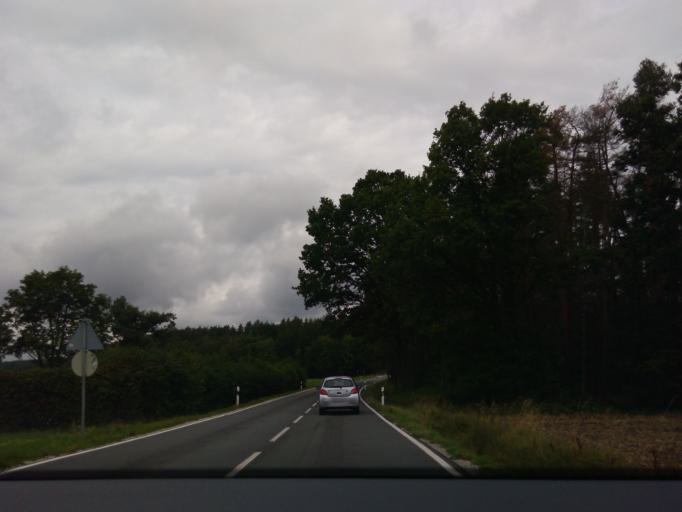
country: DE
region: Bavaria
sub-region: Regierungsbezirk Mittelfranken
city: Weisendorf
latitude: 49.6428
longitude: 10.8177
